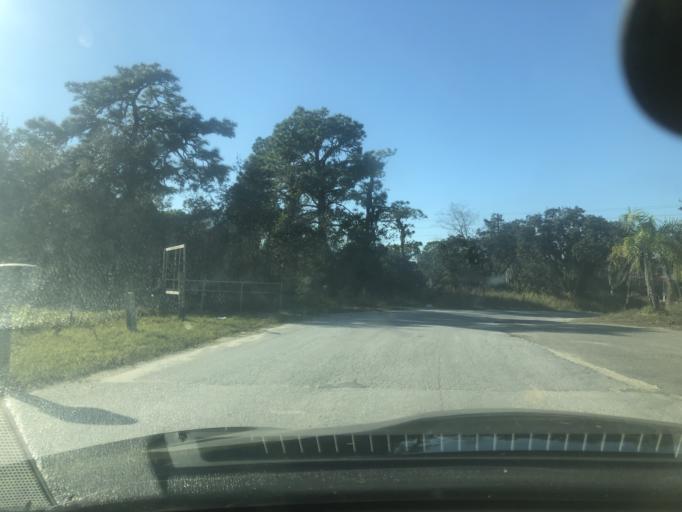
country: US
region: Florida
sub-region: Citrus County
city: Lecanto
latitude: 28.8259
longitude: -82.5250
